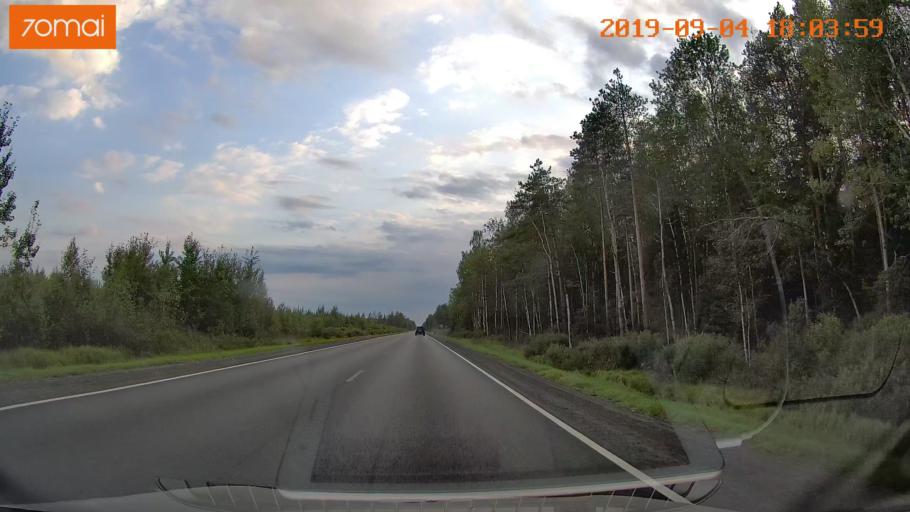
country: RU
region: Moskovskaya
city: Il'inskiy Pogost
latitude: 55.4575
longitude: 38.8452
